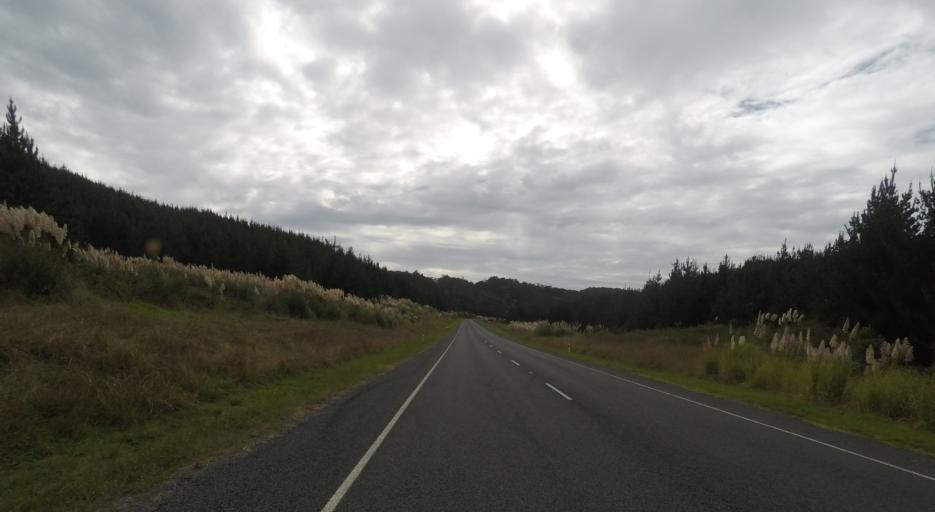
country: NZ
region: Auckland
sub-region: Auckland
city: Rothesay Bay
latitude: -36.6533
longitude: 174.7052
